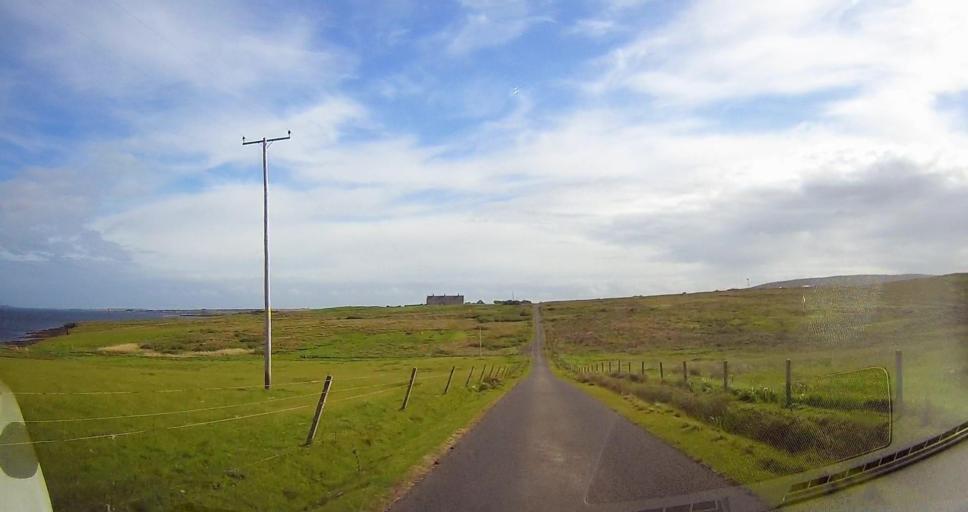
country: GB
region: Scotland
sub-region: Orkney Islands
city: Stromness
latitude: 58.8523
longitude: -3.2034
